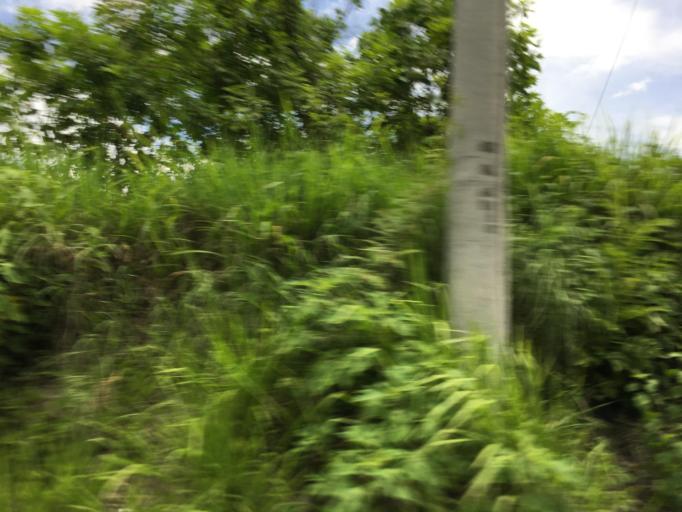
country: GT
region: Guatemala
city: Amatitlan
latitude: 14.4953
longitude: -90.6238
